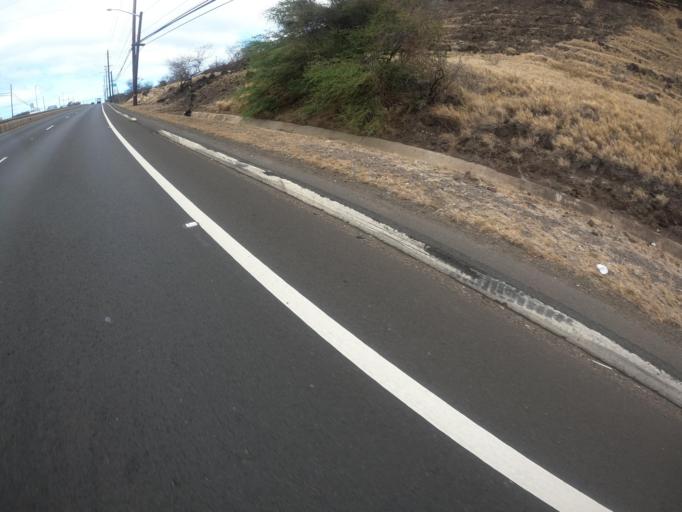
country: US
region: Hawaii
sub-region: Honolulu County
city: Ma'ili
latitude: 21.3996
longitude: -158.1732
